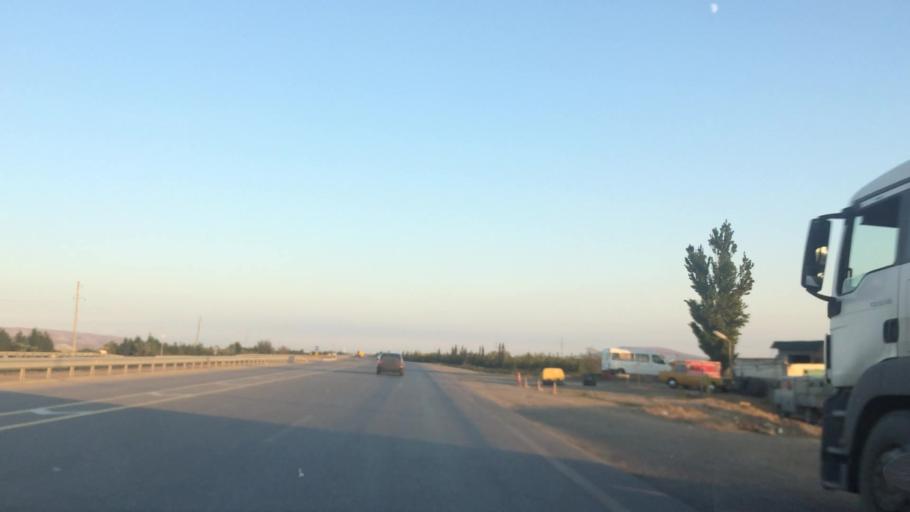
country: AZ
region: Haciqabul
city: Haciqabul
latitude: 40.0076
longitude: 49.1561
